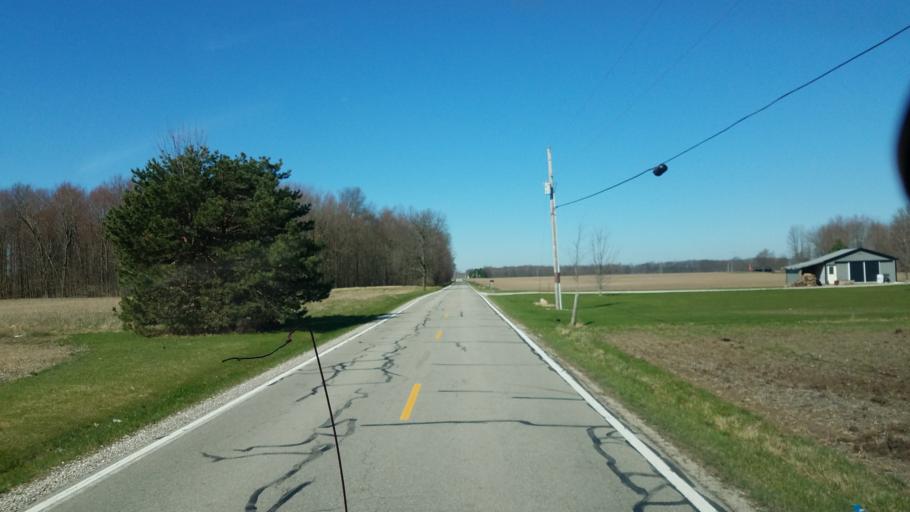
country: US
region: Ohio
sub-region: Huron County
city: Willard
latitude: 40.9820
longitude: -82.8252
